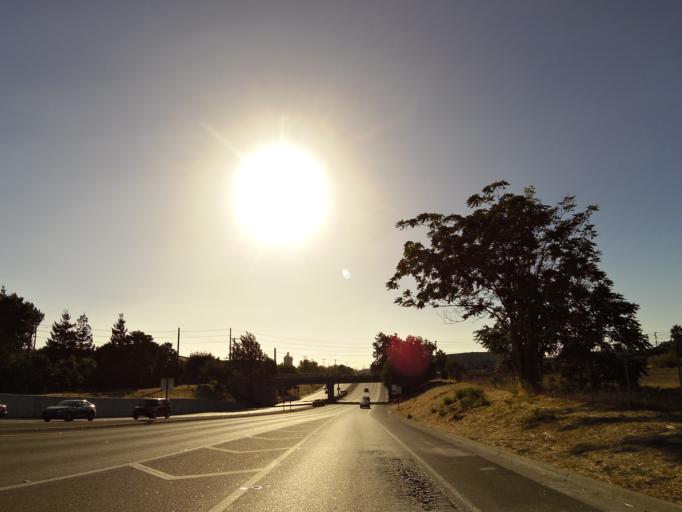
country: US
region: California
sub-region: Santa Clara County
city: Santa Clara
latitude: 37.3735
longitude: -121.9442
